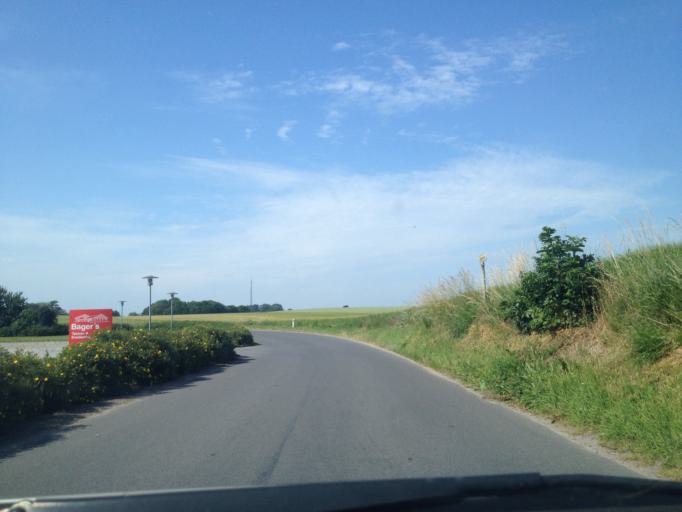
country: DK
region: Central Jutland
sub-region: Samso Kommune
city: Tranebjerg
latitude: 55.8280
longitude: 10.5611
